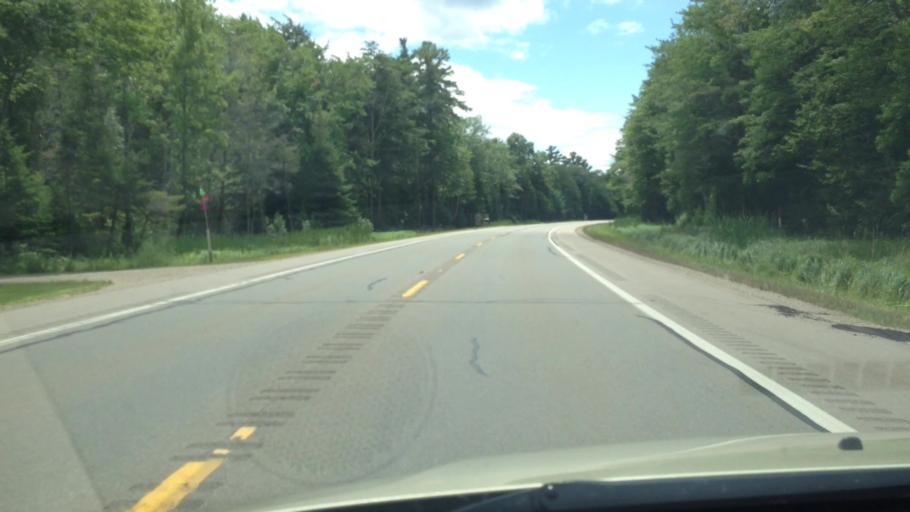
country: US
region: Michigan
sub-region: Menominee County
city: Menominee
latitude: 45.2961
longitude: -87.4403
